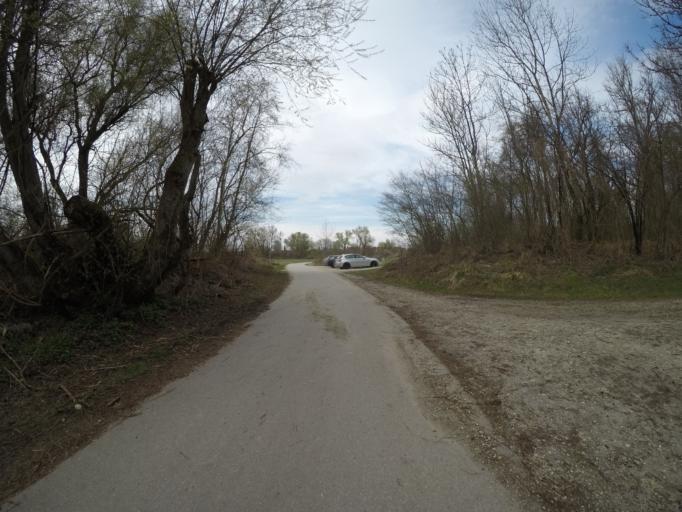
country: DE
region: Bavaria
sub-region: Lower Bavaria
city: Essenbach
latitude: 48.5879
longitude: 12.2308
